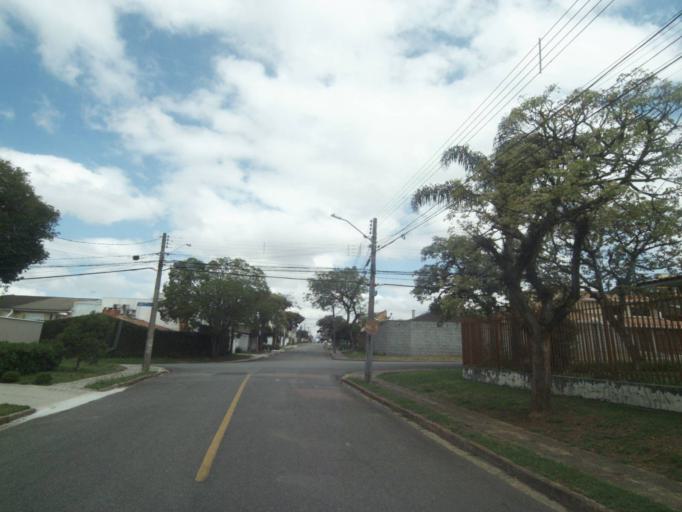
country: BR
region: Parana
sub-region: Pinhais
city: Pinhais
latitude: -25.4138
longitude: -49.2267
